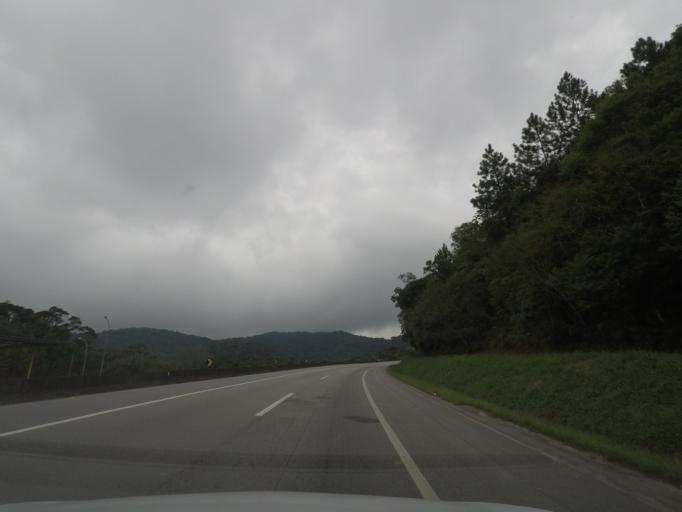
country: BR
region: Sao Paulo
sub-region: Juquitiba
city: Juquitiba
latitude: -24.0264
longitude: -47.1734
